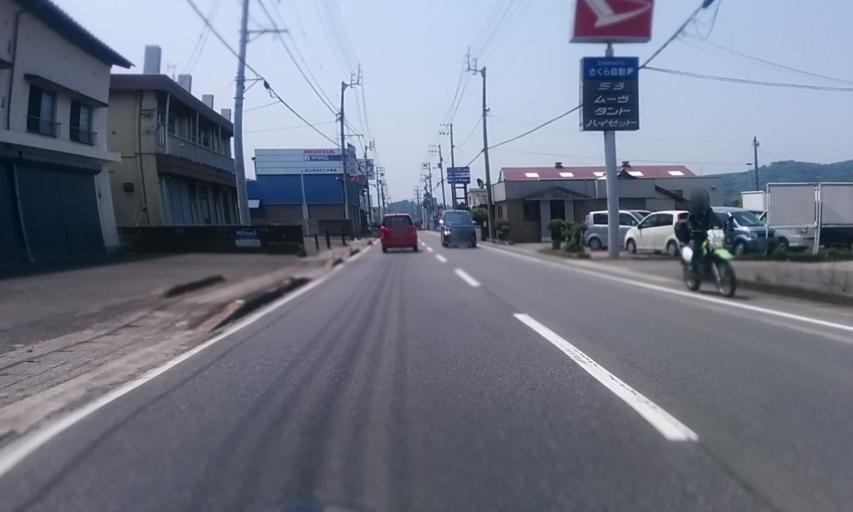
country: JP
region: Ehime
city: Niihama
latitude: 33.9300
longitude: 133.2756
